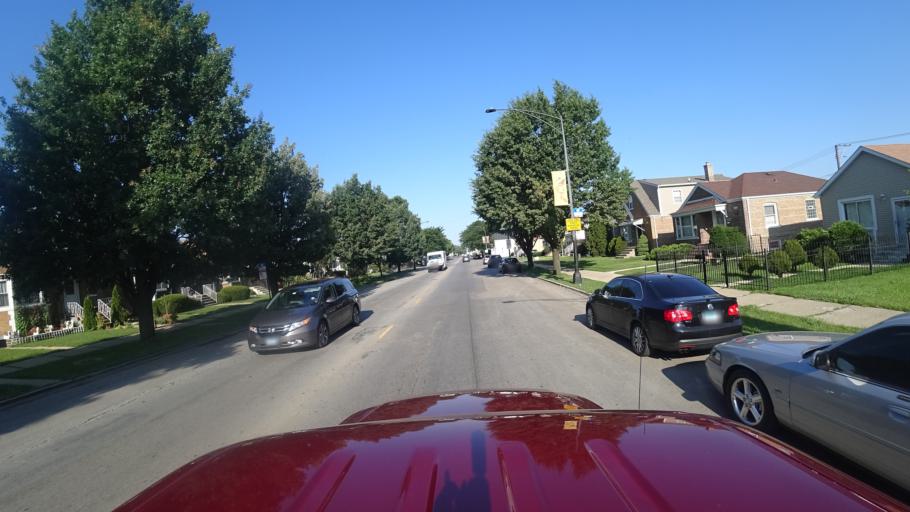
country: US
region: Illinois
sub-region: Cook County
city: Hometown
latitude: 41.7933
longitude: -87.7196
